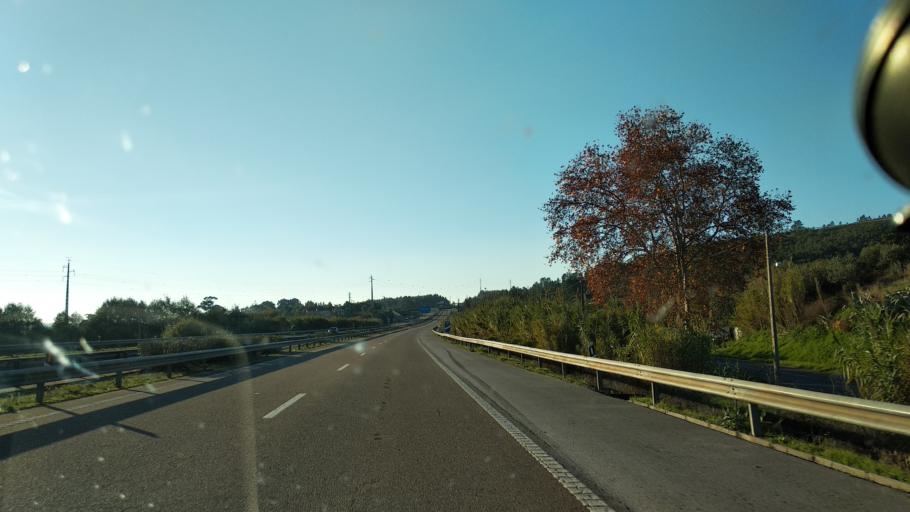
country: PT
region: Santarem
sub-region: Abrantes
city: Tramagal
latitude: 39.4864
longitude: -8.2675
